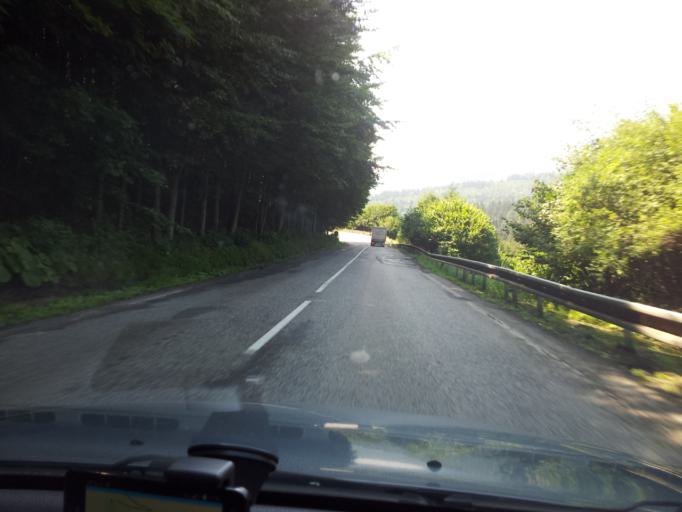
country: SK
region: Zilinsky
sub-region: Okres Dolny Kubin
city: Dolny Kubin
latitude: 49.2958
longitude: 19.3505
